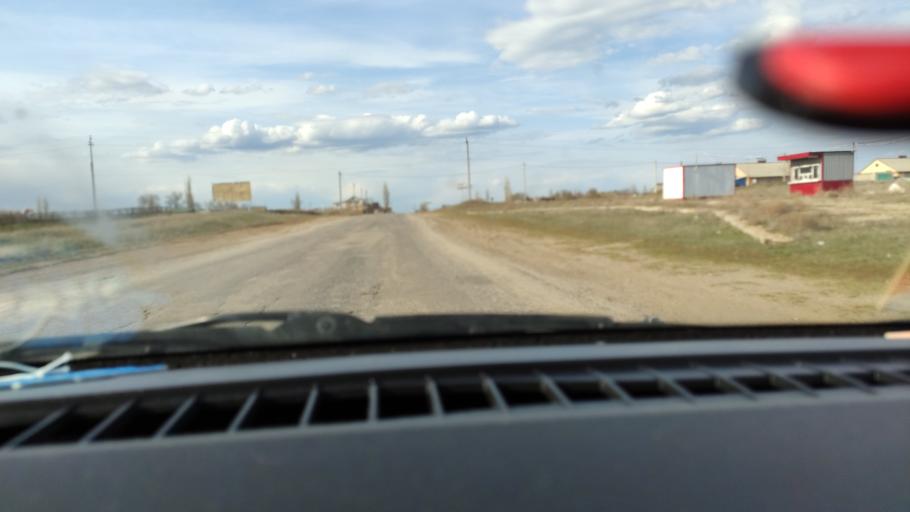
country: RU
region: Saratov
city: Rovnoye
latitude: 51.0249
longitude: 46.0931
